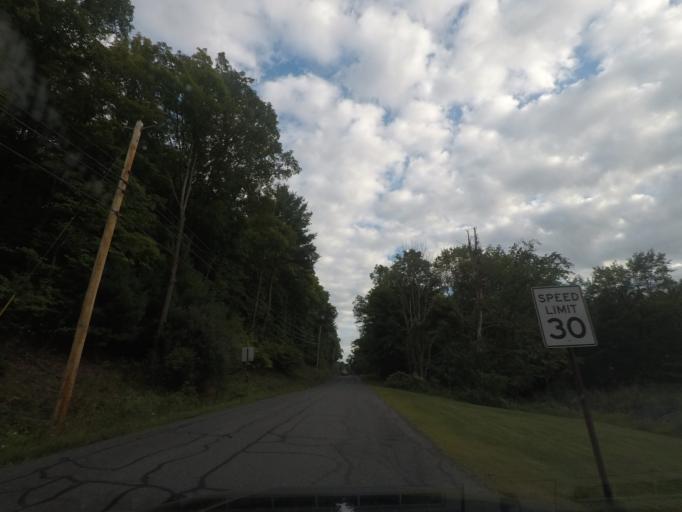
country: US
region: New York
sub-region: Rensselaer County
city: Nassau
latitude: 42.5117
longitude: -73.6089
